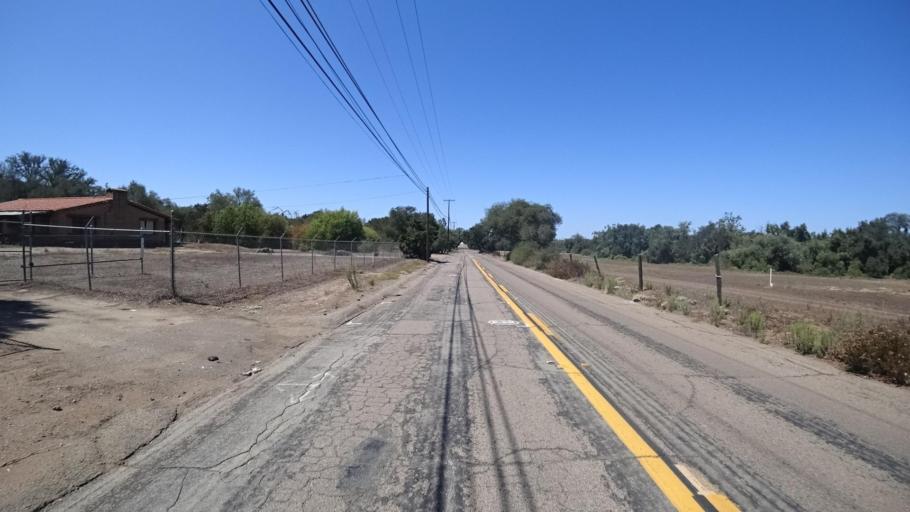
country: US
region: California
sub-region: San Diego County
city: Valley Center
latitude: 33.2673
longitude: -117.0194
